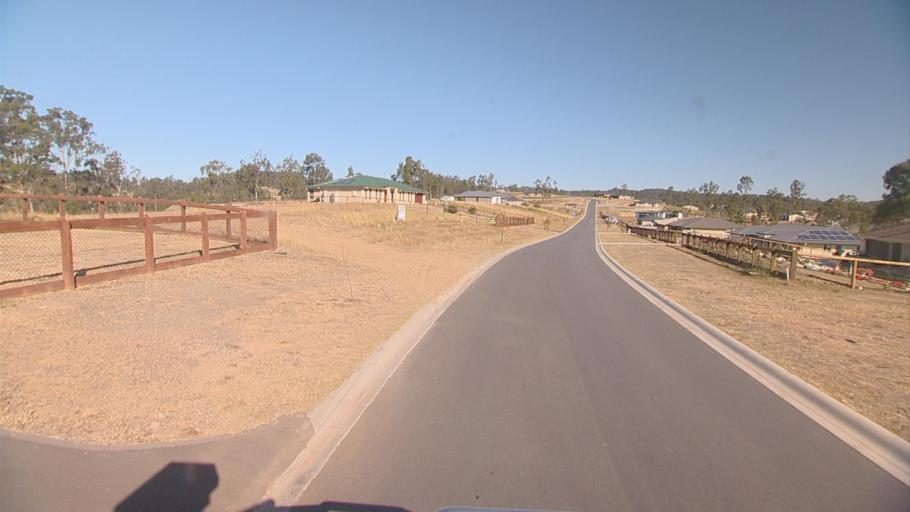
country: AU
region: Queensland
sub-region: Logan
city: Cedar Vale
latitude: -27.8679
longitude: 153.0531
